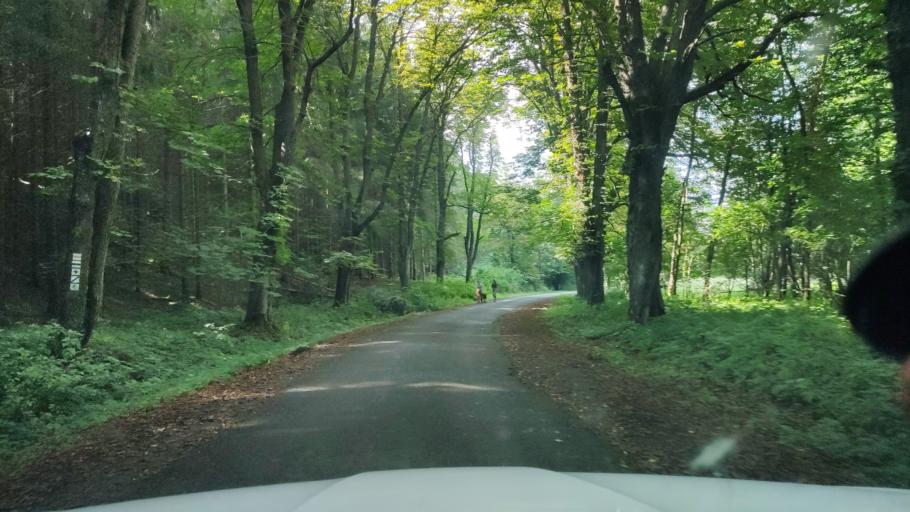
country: HU
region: Heves
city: Parad
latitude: 47.9026
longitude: 20.0560
